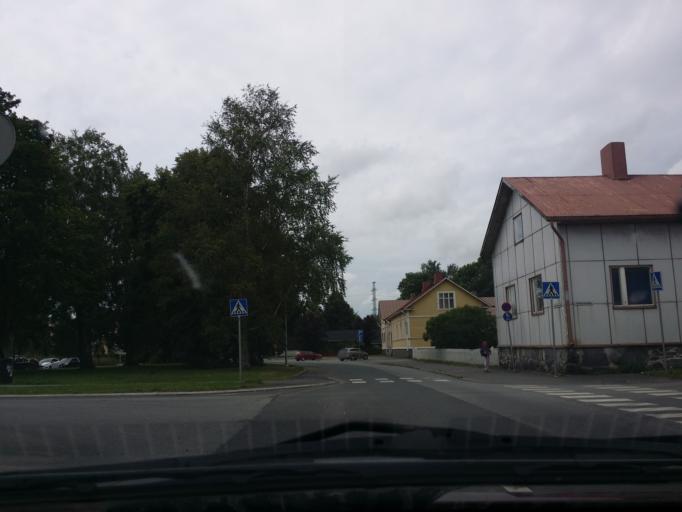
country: FI
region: Satakunta
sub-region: Pori
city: Pori
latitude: 61.4964
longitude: 21.7988
